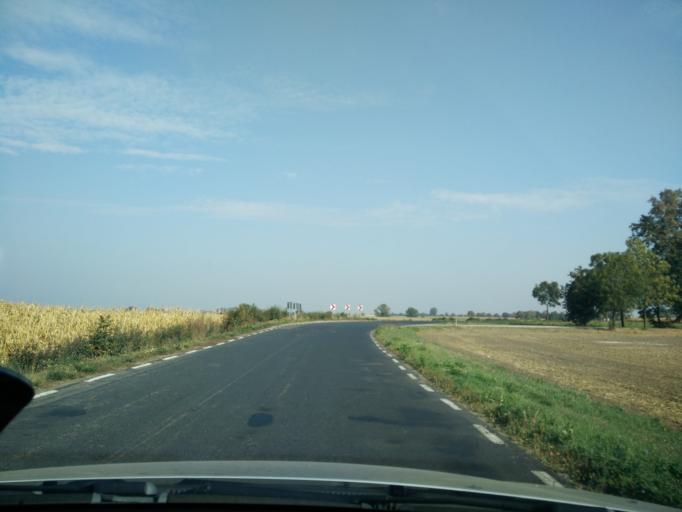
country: PL
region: Greater Poland Voivodeship
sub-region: Powiat sredzki
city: Sroda Wielkopolska
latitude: 52.2632
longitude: 17.3056
